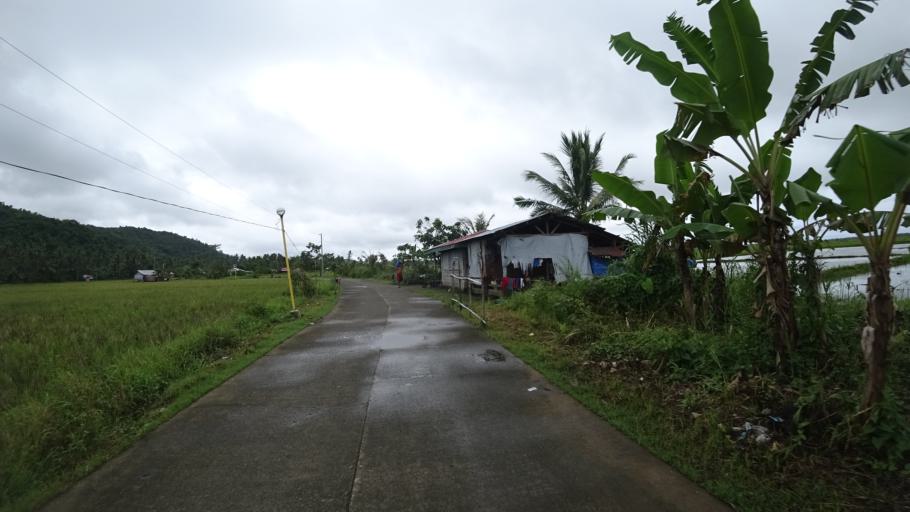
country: PH
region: Eastern Visayas
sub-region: Province of Leyte
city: Bugho
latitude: 10.7939
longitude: 124.9734
